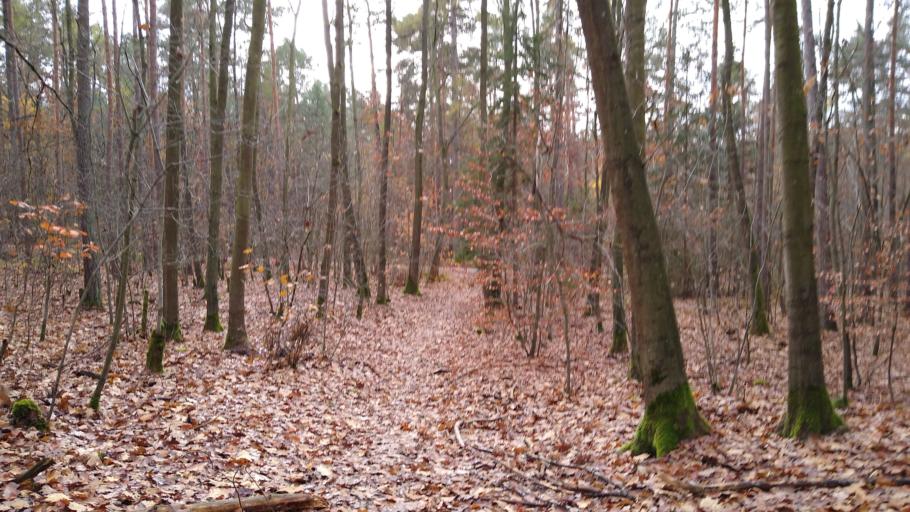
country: DE
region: Bavaria
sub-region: Regierungsbezirk Mittelfranken
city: Kalchreuth
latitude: 49.5455
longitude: 11.1155
